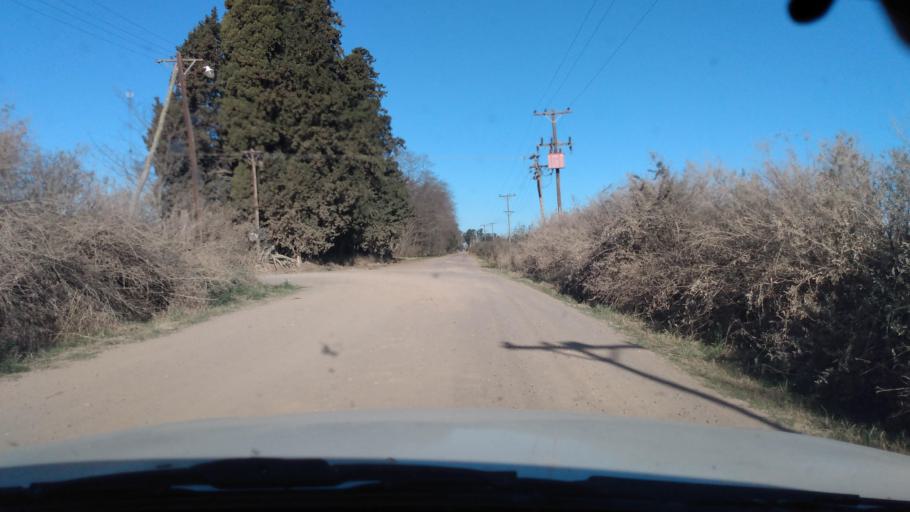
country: AR
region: Buenos Aires
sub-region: Partido de Mercedes
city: Mercedes
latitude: -34.6402
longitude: -59.3716
